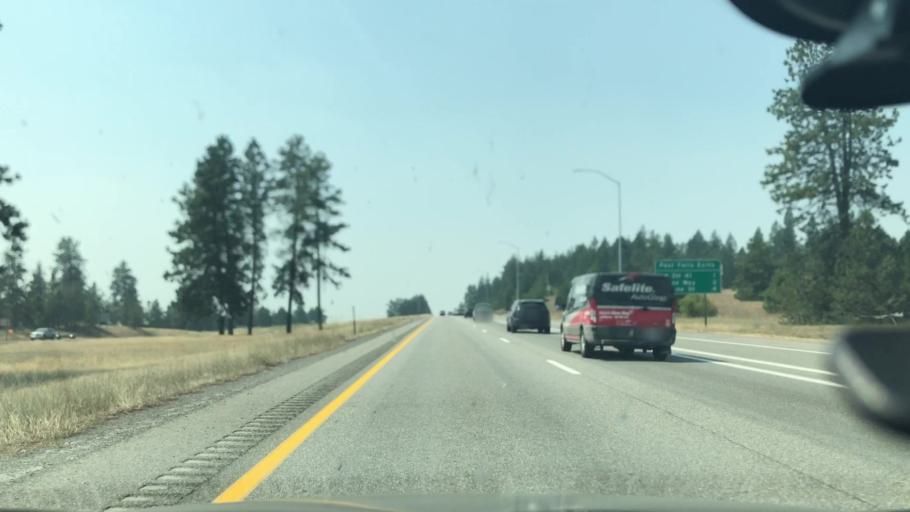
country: US
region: Idaho
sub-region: Kootenai County
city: Post Falls
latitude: 47.7093
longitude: -116.8728
